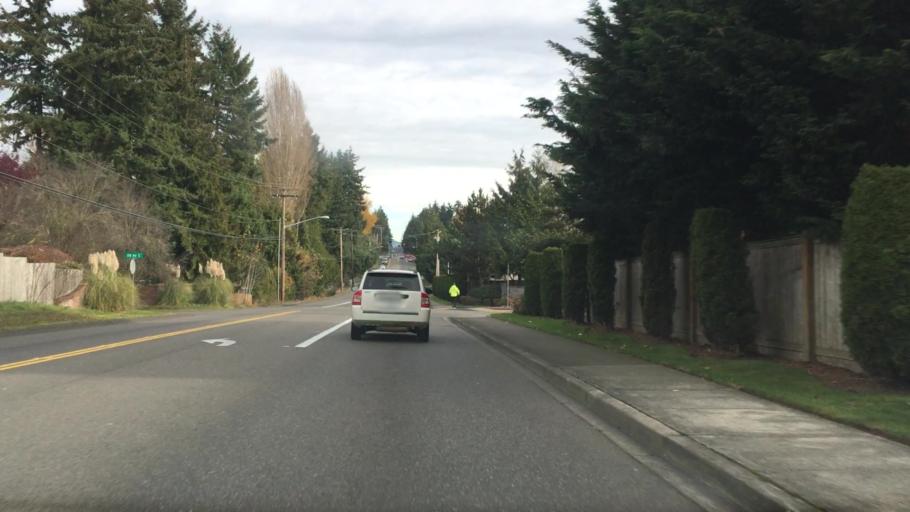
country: US
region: Washington
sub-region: Pierce County
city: Frederickson
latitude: 47.1111
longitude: -122.3132
